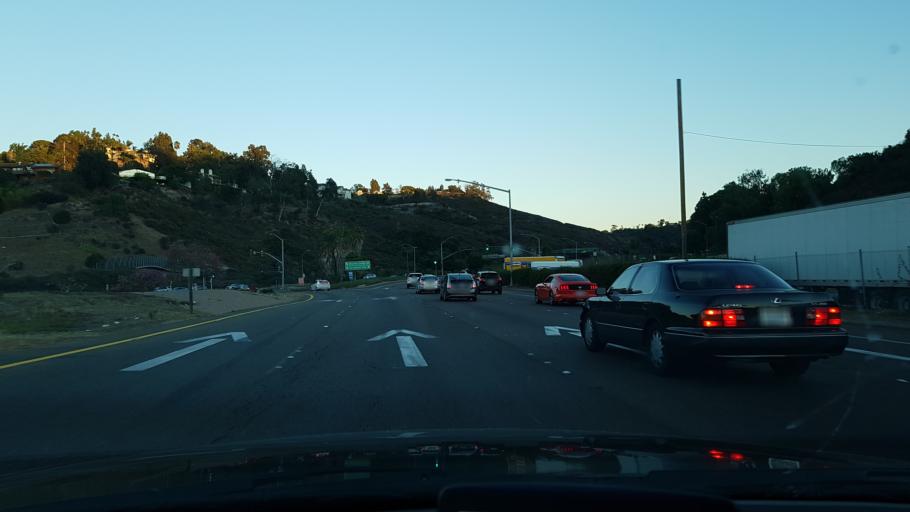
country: US
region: California
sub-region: San Diego County
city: Lemon Grove
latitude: 32.7782
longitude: -117.1023
